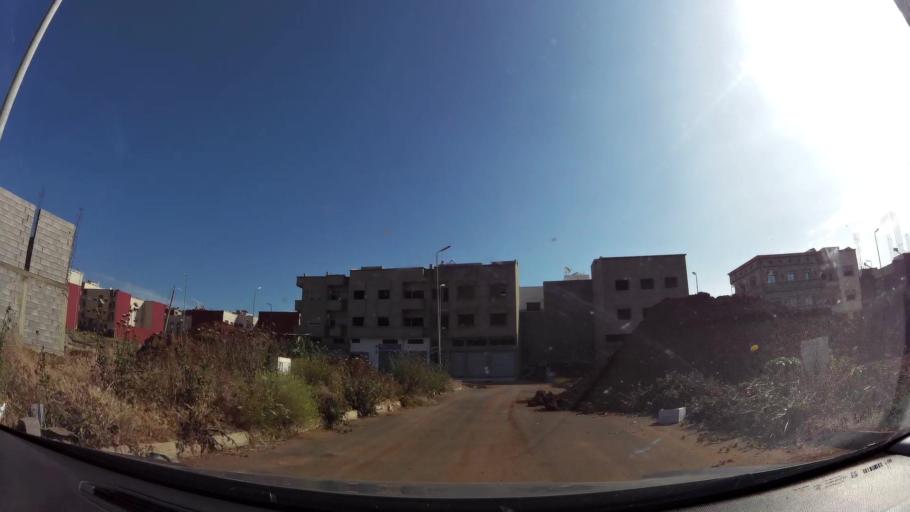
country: MA
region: Rabat-Sale-Zemmour-Zaer
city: Sale
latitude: 34.0587
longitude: -6.8091
